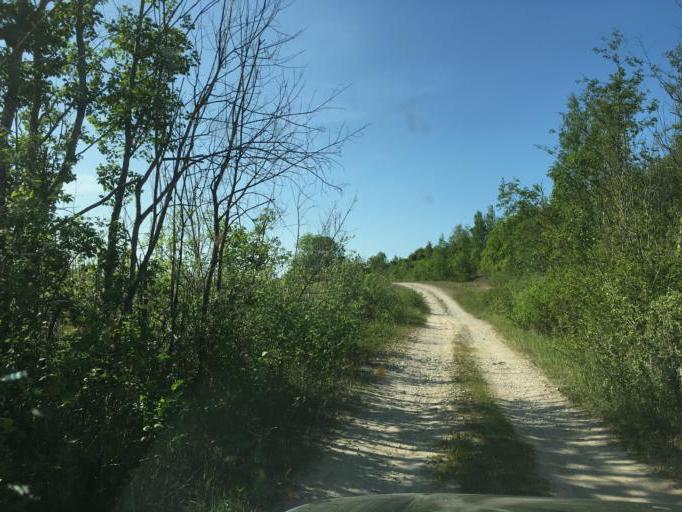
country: LV
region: Dundaga
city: Dundaga
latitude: 57.6126
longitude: 22.4387
